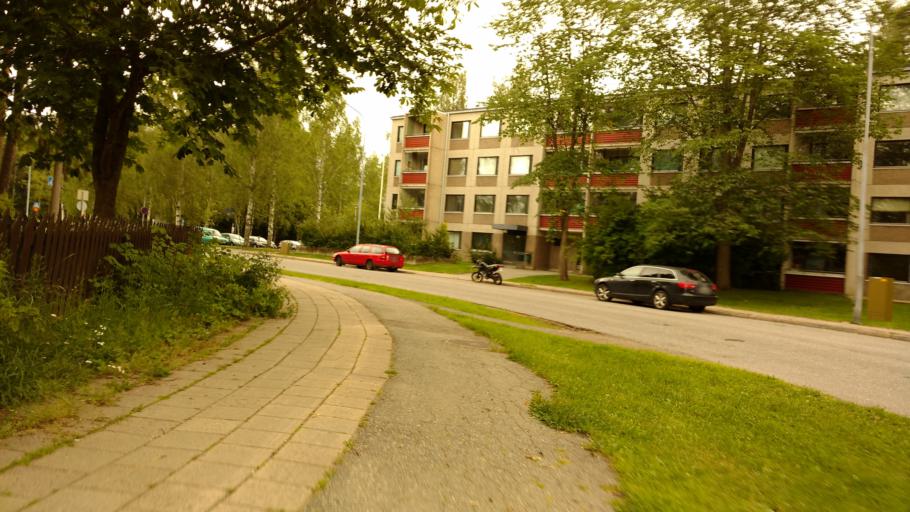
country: FI
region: Varsinais-Suomi
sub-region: Turku
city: Kaarina
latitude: 60.4421
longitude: 22.3646
